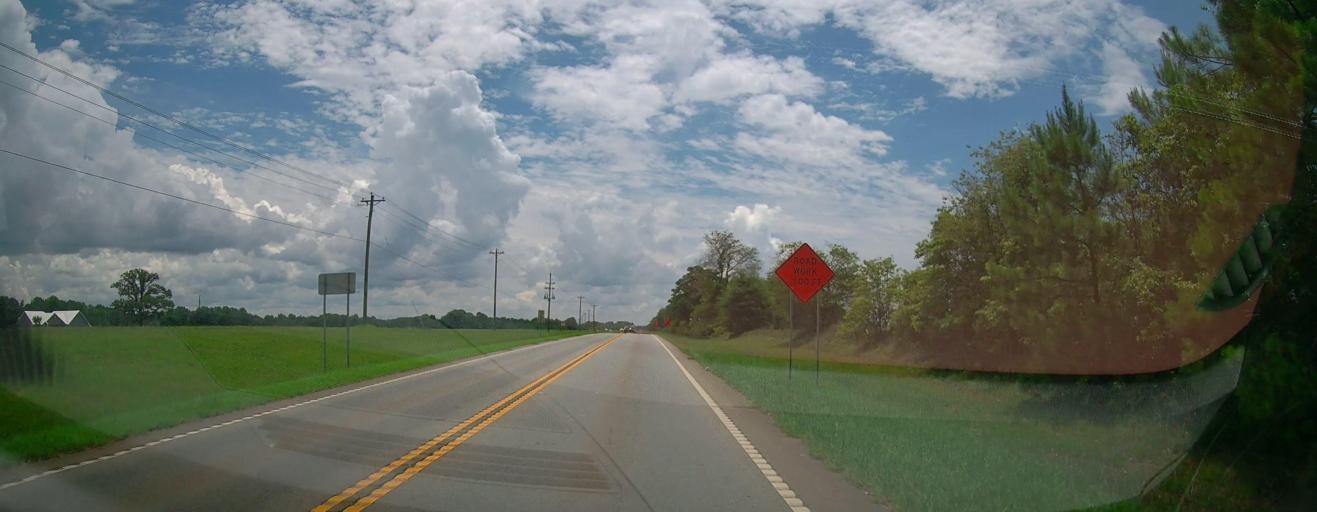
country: US
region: Georgia
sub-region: Houston County
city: Perry
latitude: 32.4756
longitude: -83.6161
